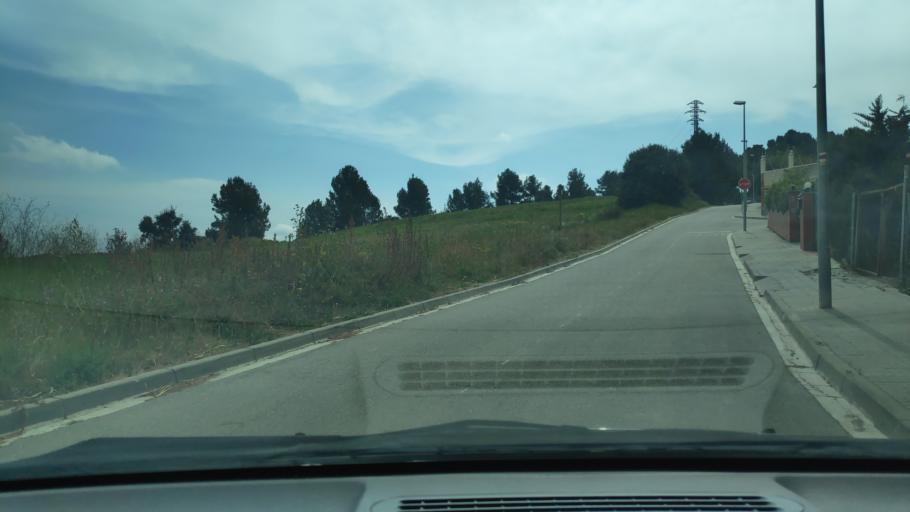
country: ES
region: Catalonia
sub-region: Provincia de Barcelona
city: Sant Quirze del Valles
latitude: 41.5152
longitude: 2.0646
